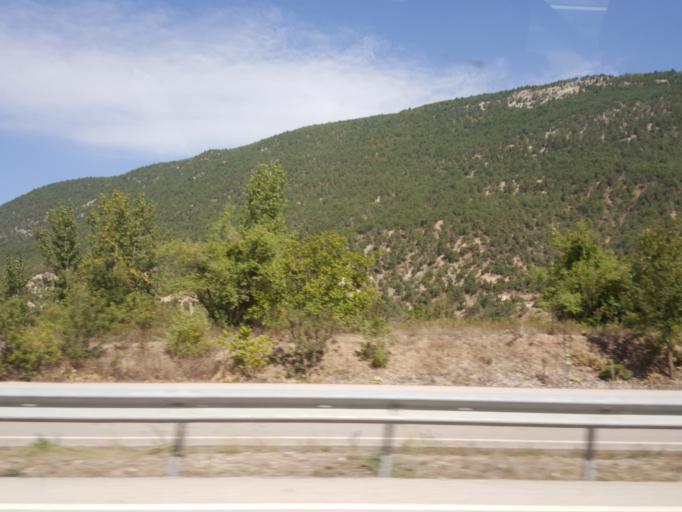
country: TR
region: Tokat
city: Basciftlik
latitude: 40.4359
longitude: 37.1153
